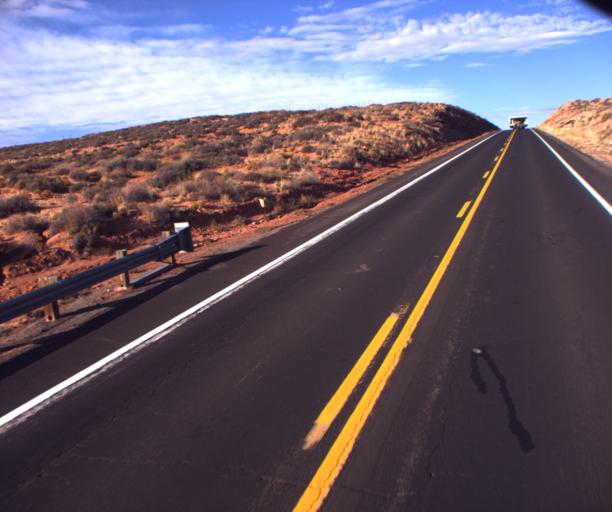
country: US
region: Arizona
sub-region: Apache County
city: Lukachukai
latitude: 36.9629
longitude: -109.4438
